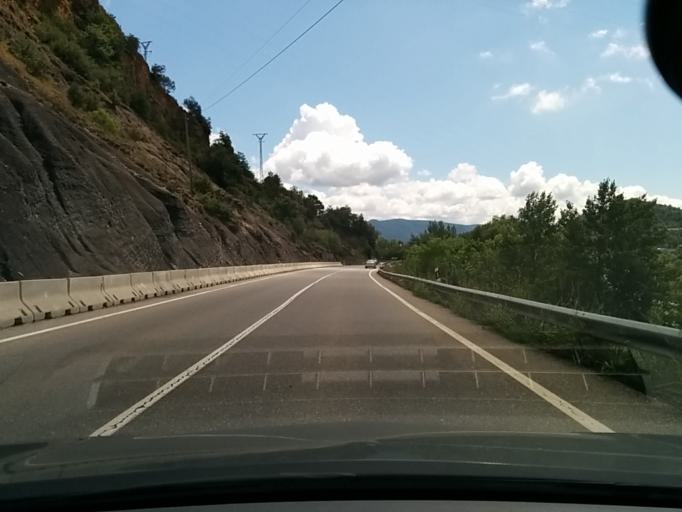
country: ES
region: Aragon
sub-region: Provincia de Huesca
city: Ainsa
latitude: 42.4181
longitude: 0.1316
